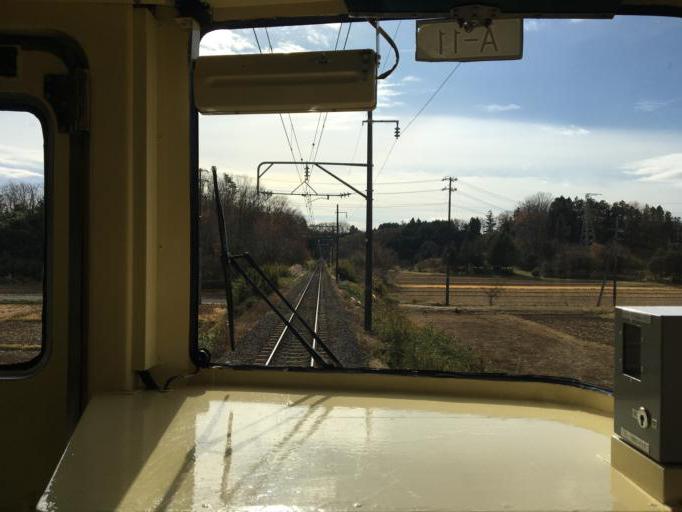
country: JP
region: Miyagi
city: Kakuda
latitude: 37.9581
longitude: 140.7701
